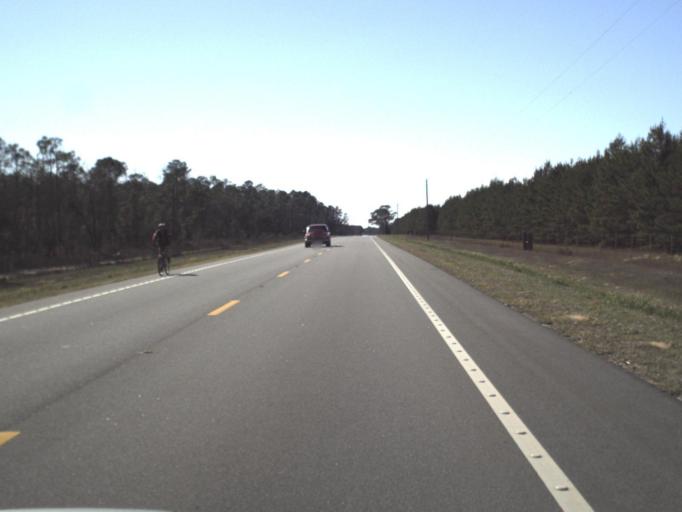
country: US
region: Florida
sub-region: Bay County
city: Youngstown
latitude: 30.4339
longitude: -85.2617
